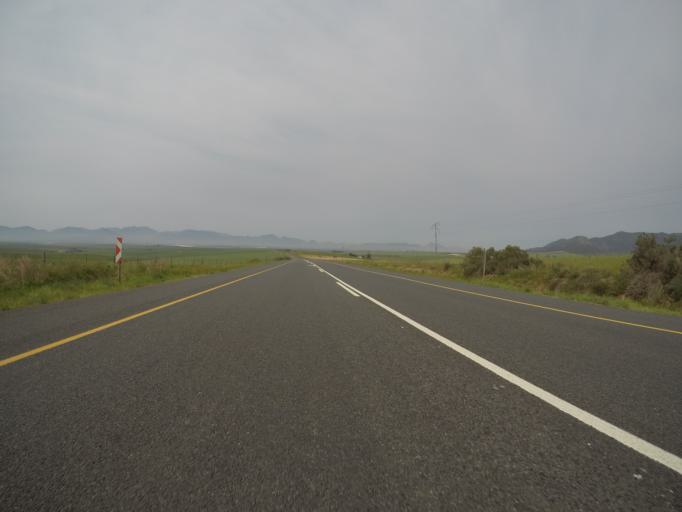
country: ZA
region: Western Cape
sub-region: West Coast District Municipality
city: Malmesbury
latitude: -33.5383
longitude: 18.8567
